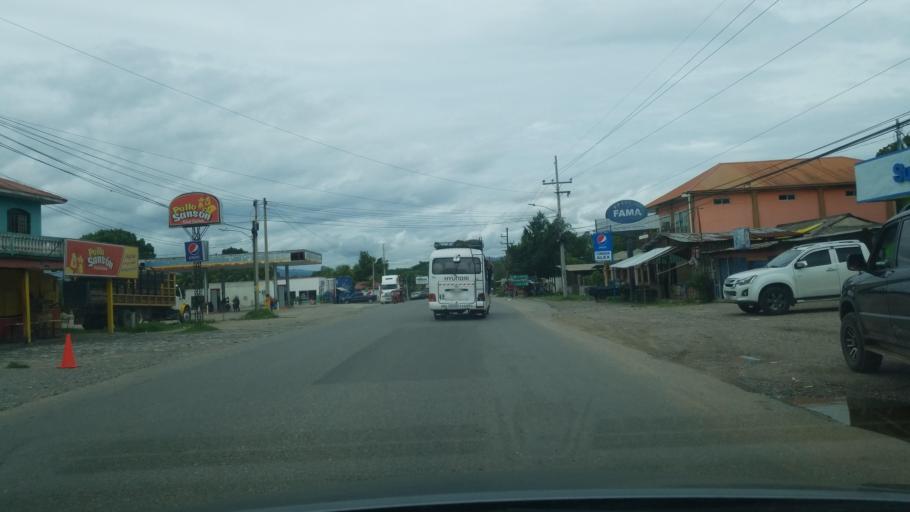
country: HN
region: Santa Barbara
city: El Ciruelo
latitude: 15.2924
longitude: -88.4927
